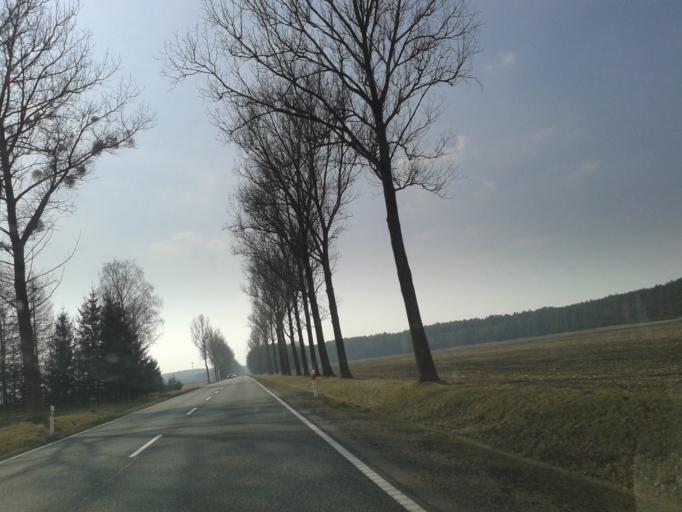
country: PL
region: Pomeranian Voivodeship
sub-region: Powiat czluchowski
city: Czarne
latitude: 53.5677
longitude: 17.0568
